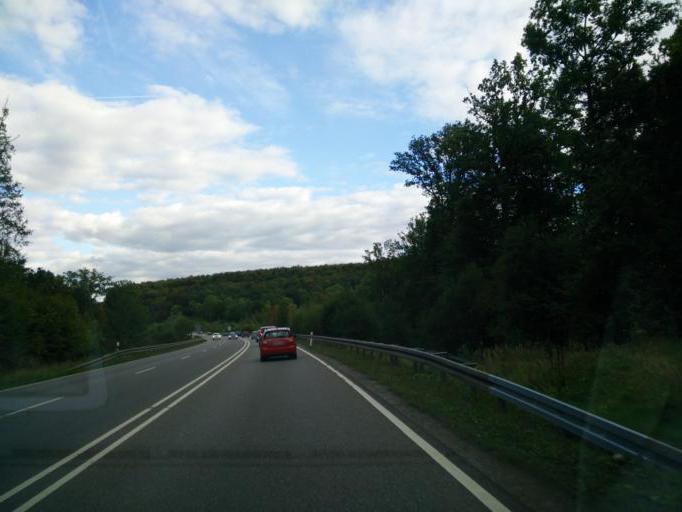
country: DE
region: Baden-Wuerttemberg
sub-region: Regierungsbezirk Stuttgart
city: Boeblingen
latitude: 48.6640
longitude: 8.9882
